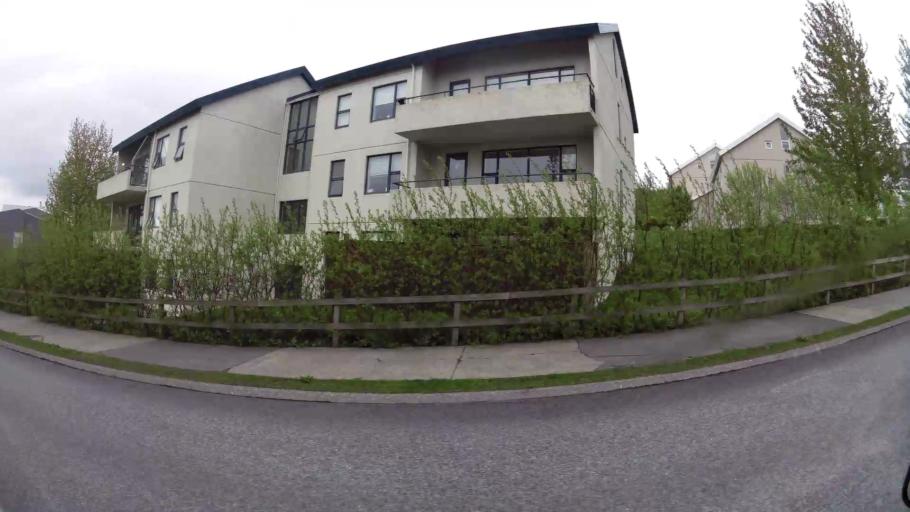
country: IS
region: Capital Region
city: Hafnarfjoerdur
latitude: 64.0649
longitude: -21.9289
